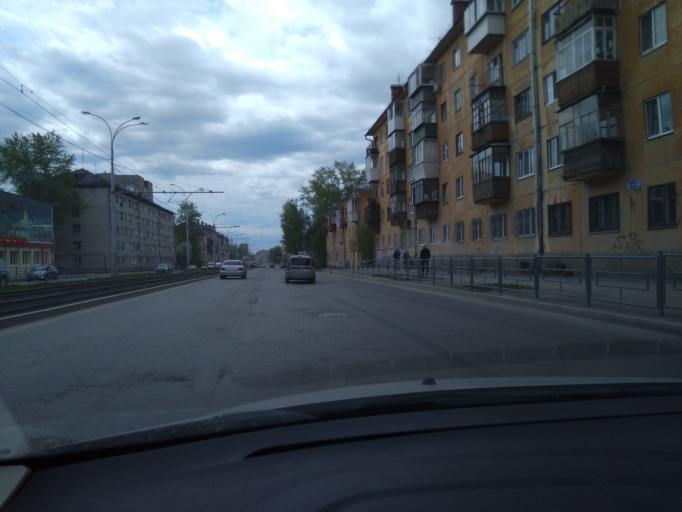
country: RU
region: Sverdlovsk
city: Yekaterinburg
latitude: 56.8871
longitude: 60.5656
